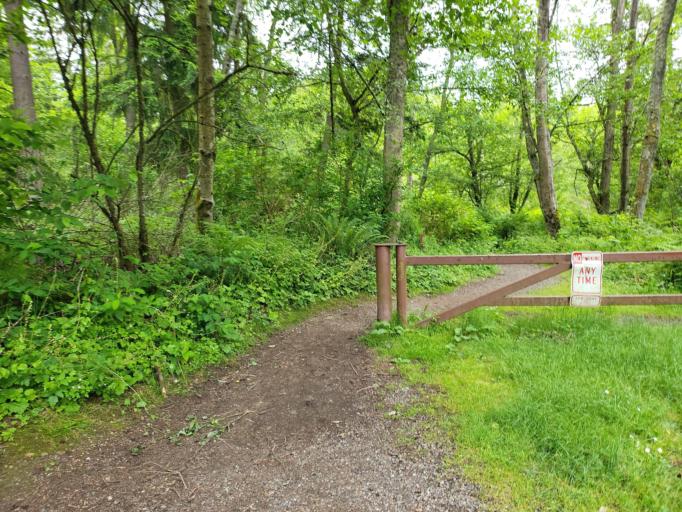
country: US
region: Washington
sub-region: Pierce County
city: Tacoma
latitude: 47.3145
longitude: -122.4038
